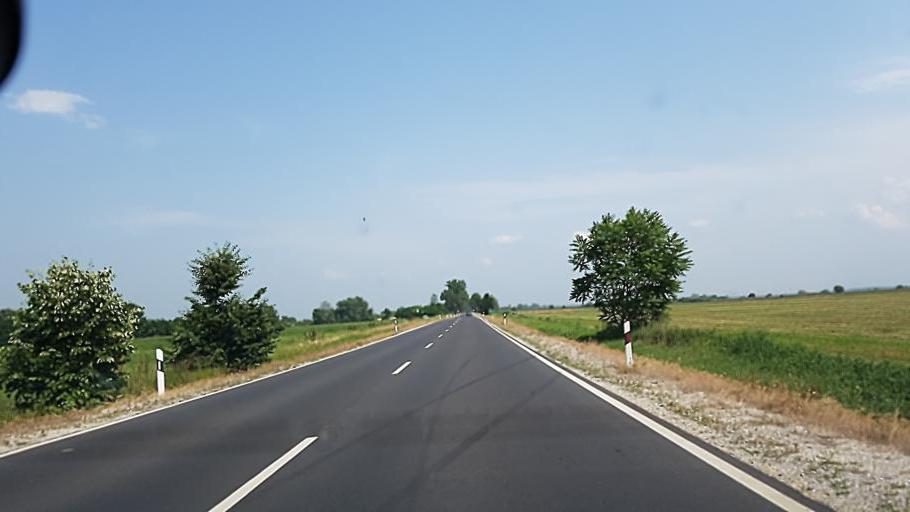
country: HU
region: Heves
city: Tiszanana
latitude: 47.6735
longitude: 20.5383
